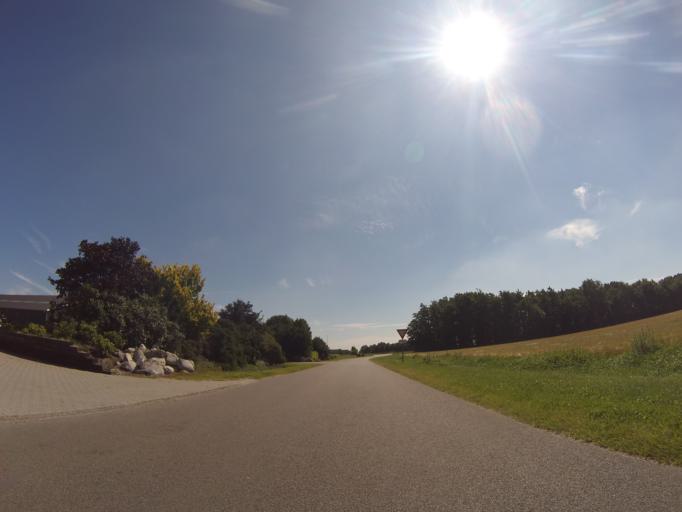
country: NL
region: Drenthe
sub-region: Gemeente Emmen
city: Klazienaveen
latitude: 52.6888
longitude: 6.9748
